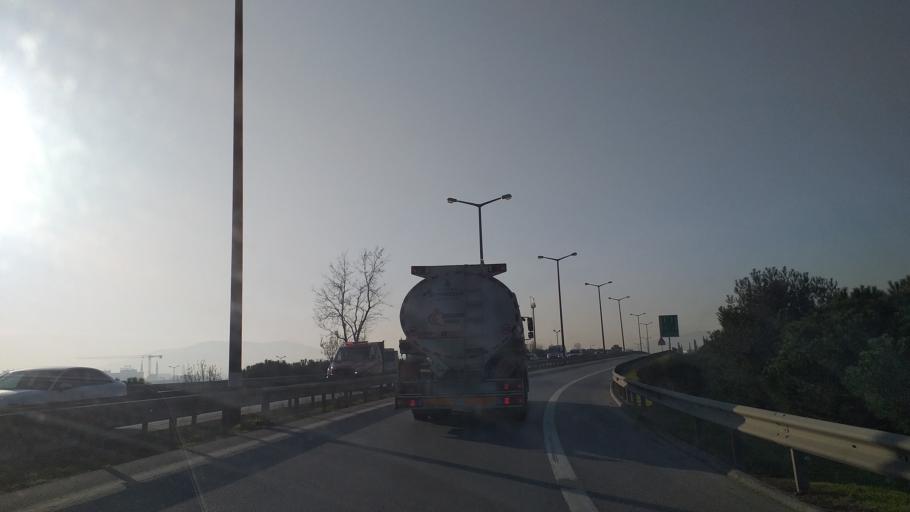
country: TR
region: Istanbul
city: Samandira
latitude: 40.9843
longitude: 29.2058
